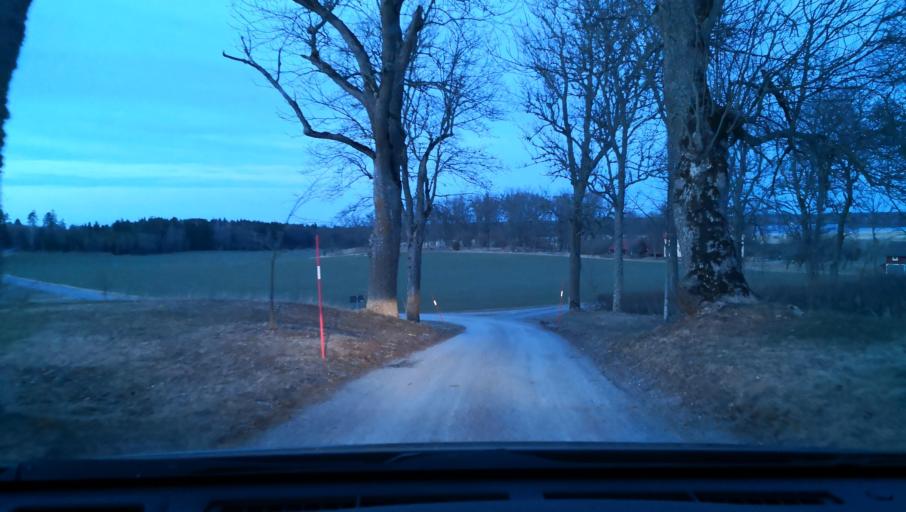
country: SE
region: Uppsala
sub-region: Enkopings Kommun
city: Dalby
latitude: 59.5573
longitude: 17.3707
